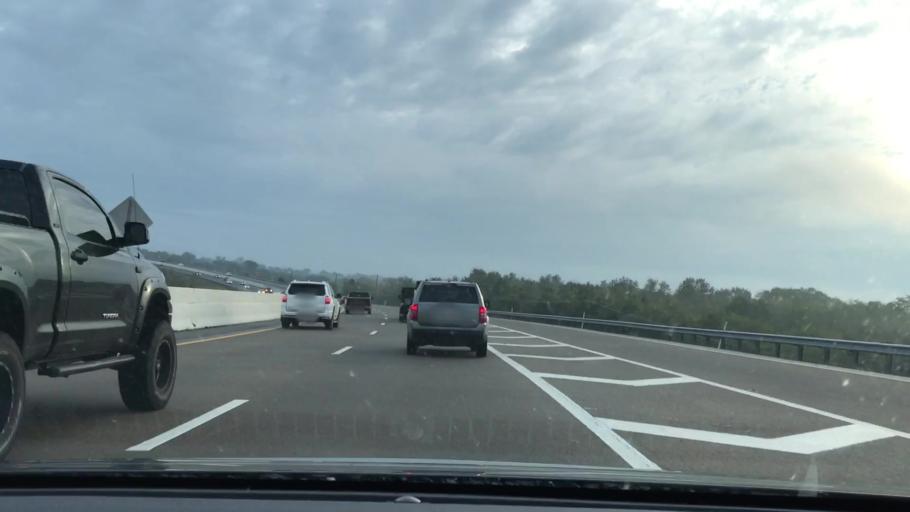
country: US
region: Tennessee
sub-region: Sumner County
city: Hendersonville
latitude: 36.3289
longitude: -86.5543
